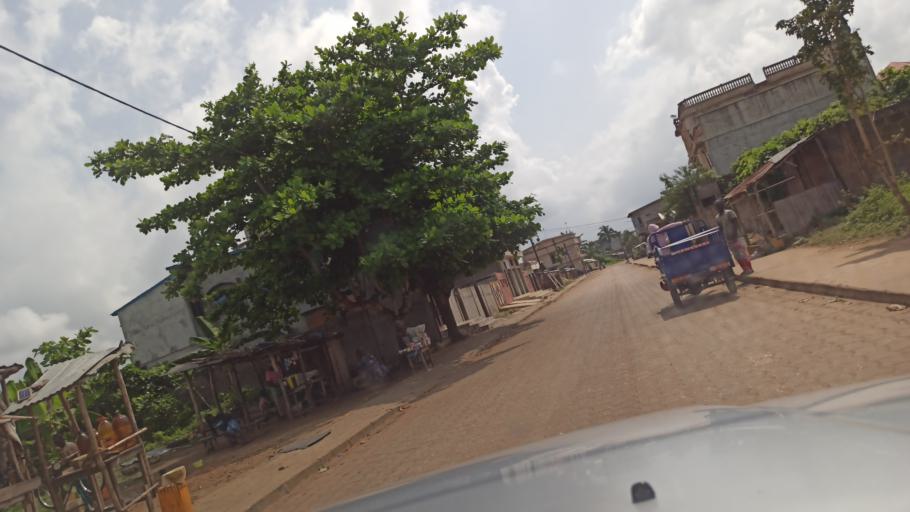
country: BJ
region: Queme
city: Porto-Novo
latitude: 6.4665
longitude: 2.6535
